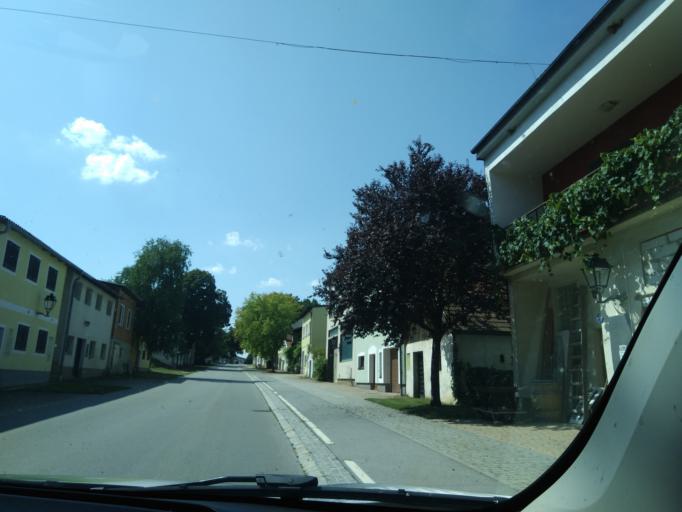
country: AT
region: Lower Austria
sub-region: Politischer Bezirk Ganserndorf
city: Auersthal
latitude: 48.3756
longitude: 16.6290
